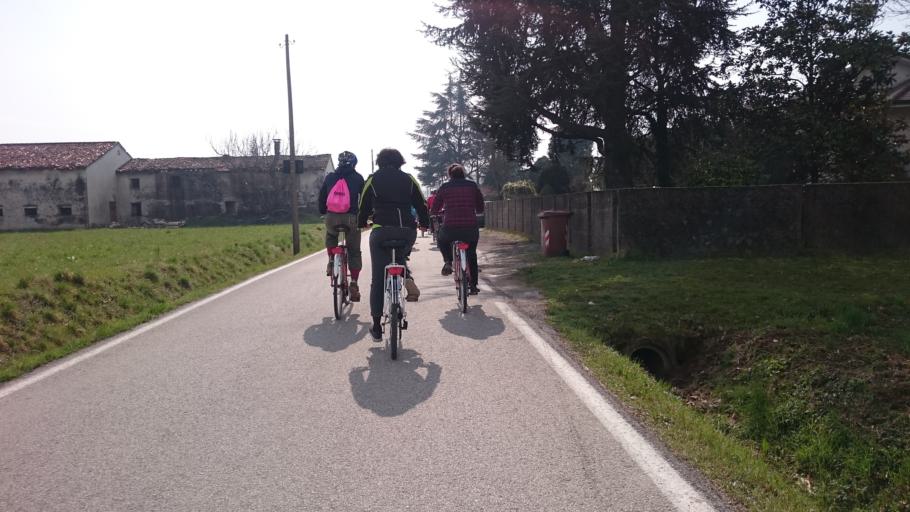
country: IT
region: Veneto
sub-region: Provincia di Vicenza
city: Villaganzerla
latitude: 45.4481
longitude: 11.6197
